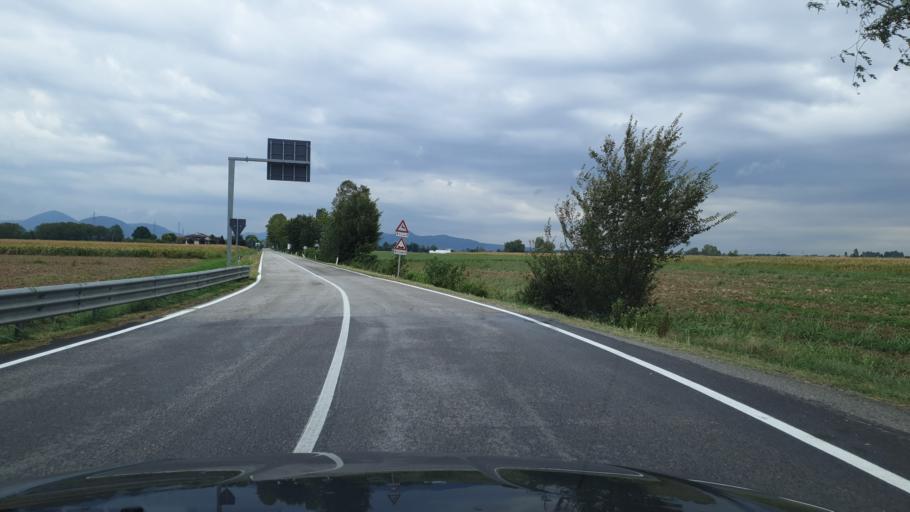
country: IT
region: Veneto
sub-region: Provincia di Vicenza
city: Noventa Vicentina
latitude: 45.2763
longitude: 11.5518
